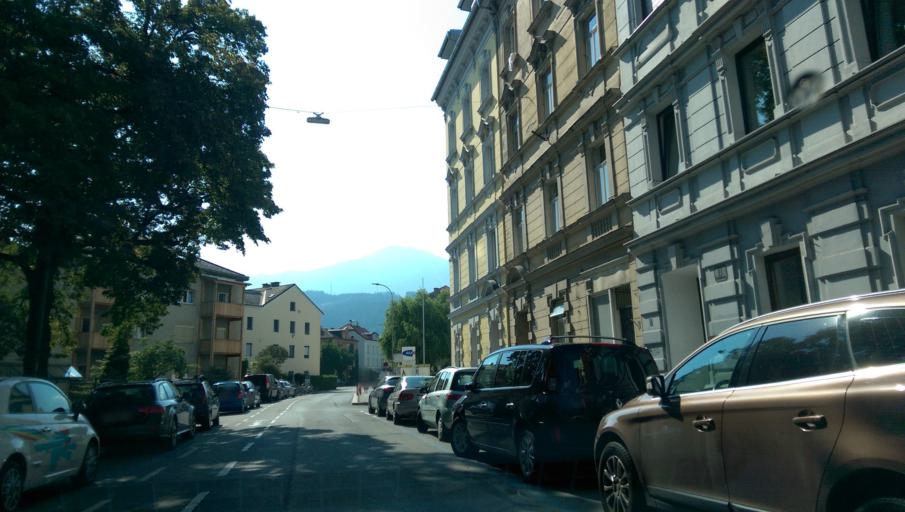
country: AT
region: Tyrol
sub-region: Innsbruck Stadt
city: Innsbruck
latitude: 47.2598
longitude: 11.3925
